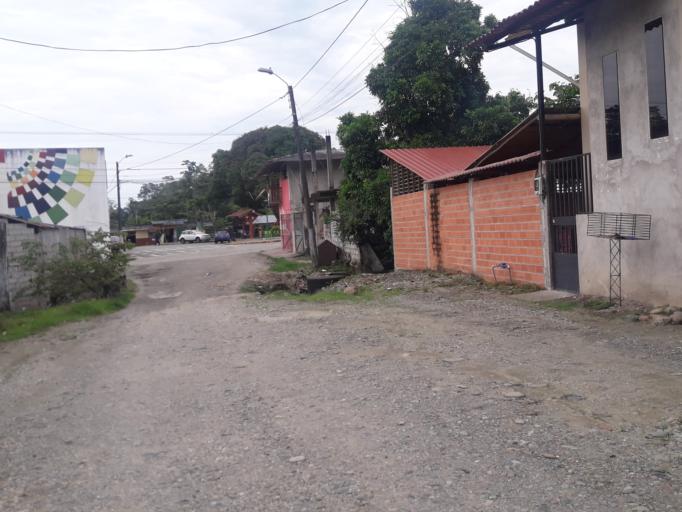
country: EC
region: Napo
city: Tena
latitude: -1.0419
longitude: -77.7946
